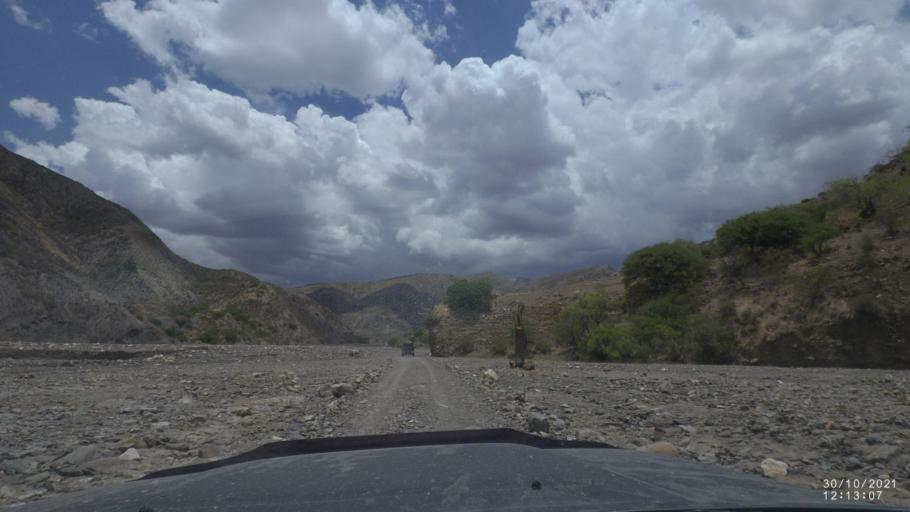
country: BO
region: Cochabamba
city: Colchani
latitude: -17.5561
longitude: -66.6228
